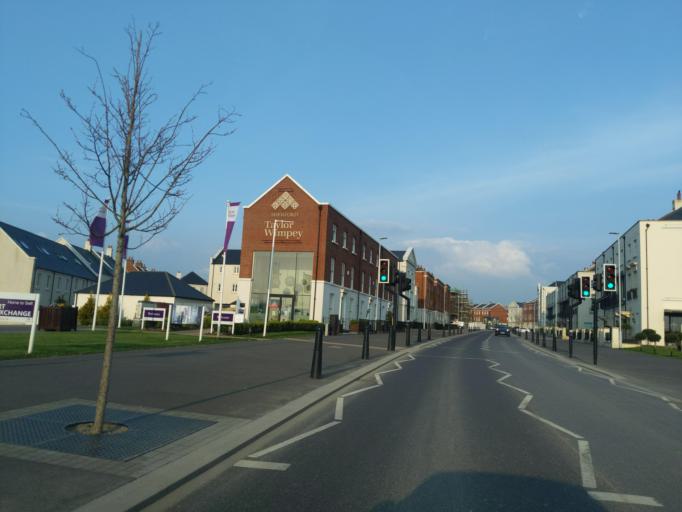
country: GB
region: England
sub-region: Devon
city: Plympton
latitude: 50.3658
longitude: -4.0553
